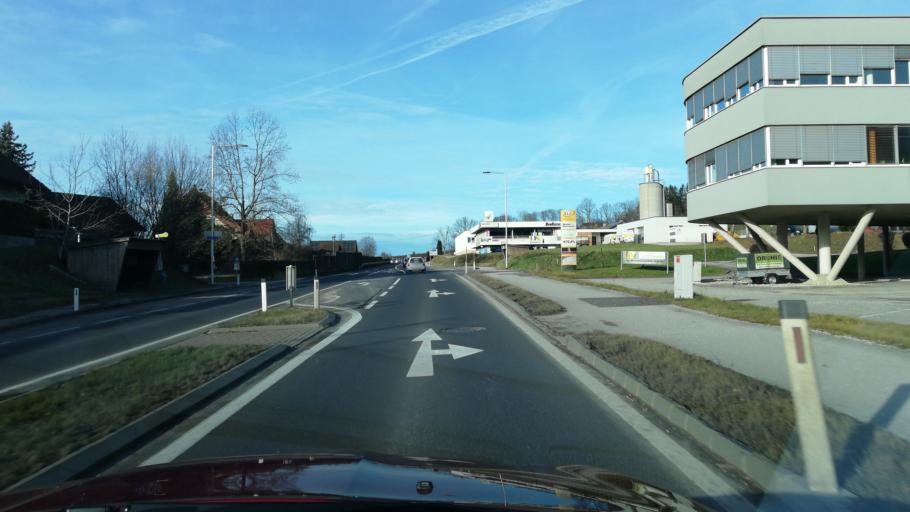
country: AT
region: Upper Austria
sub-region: Politischer Bezirk Kirchdorf an der Krems
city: Micheldorf in Oberoesterreich
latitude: 47.9156
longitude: 14.1104
